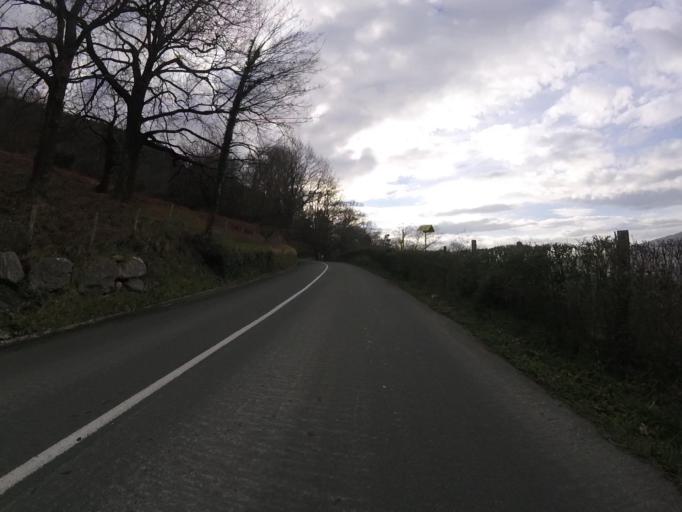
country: ES
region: Basque Country
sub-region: Provincia de Guipuzcoa
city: Irun
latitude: 43.3243
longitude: -1.8179
